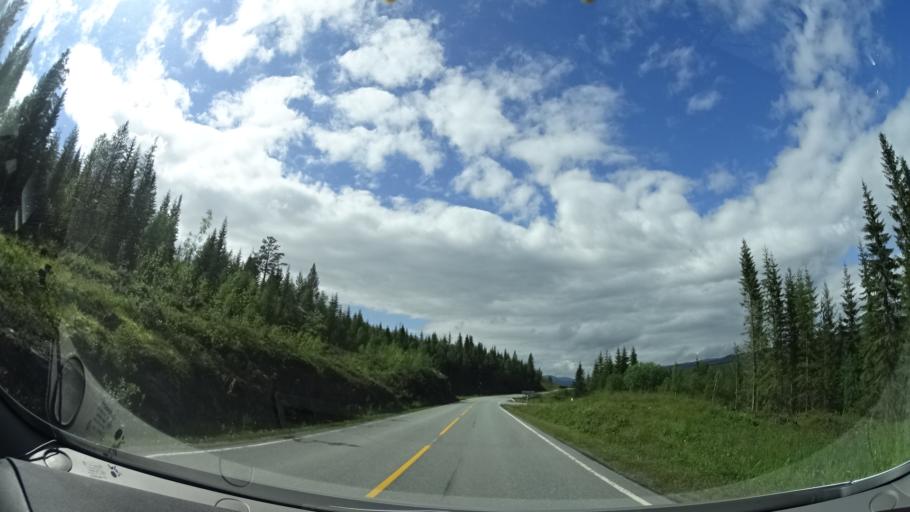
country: NO
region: Nord-Trondelag
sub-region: Meraker
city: Meraker
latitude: 63.3791
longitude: 11.8930
